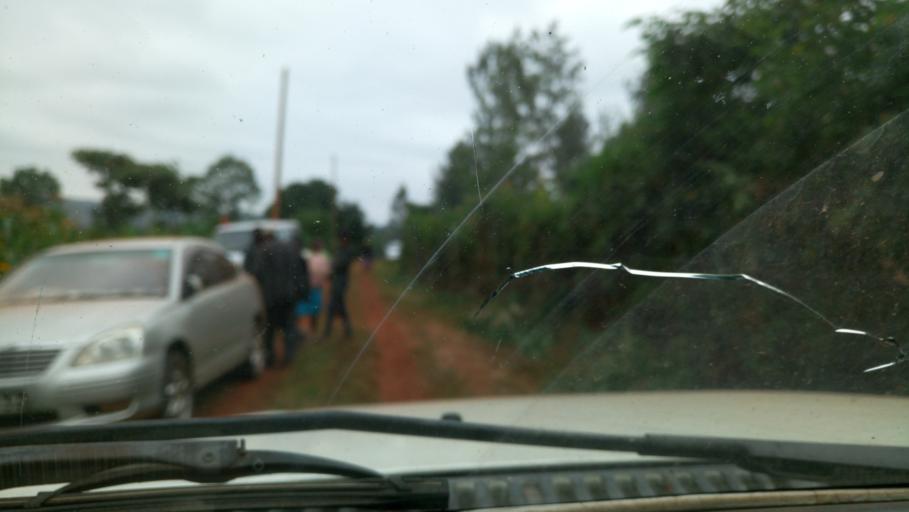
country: KE
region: Murang'a District
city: Murang'a
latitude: -0.7193
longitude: 37.0959
